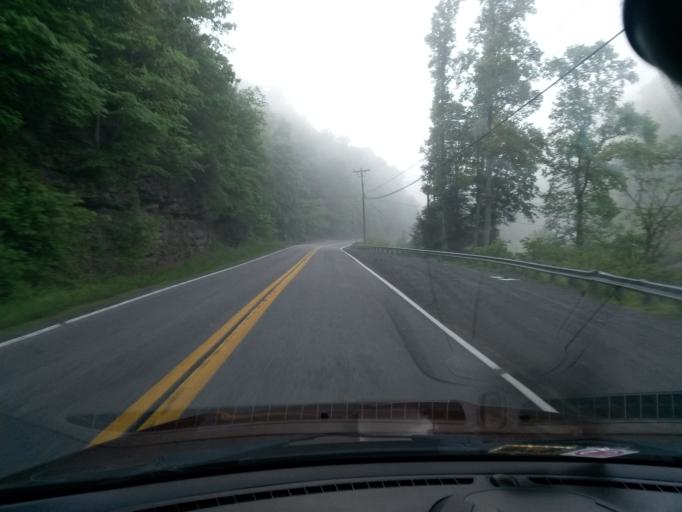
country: US
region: West Virginia
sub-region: McDowell County
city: Welch
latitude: 37.4781
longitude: -81.5446
